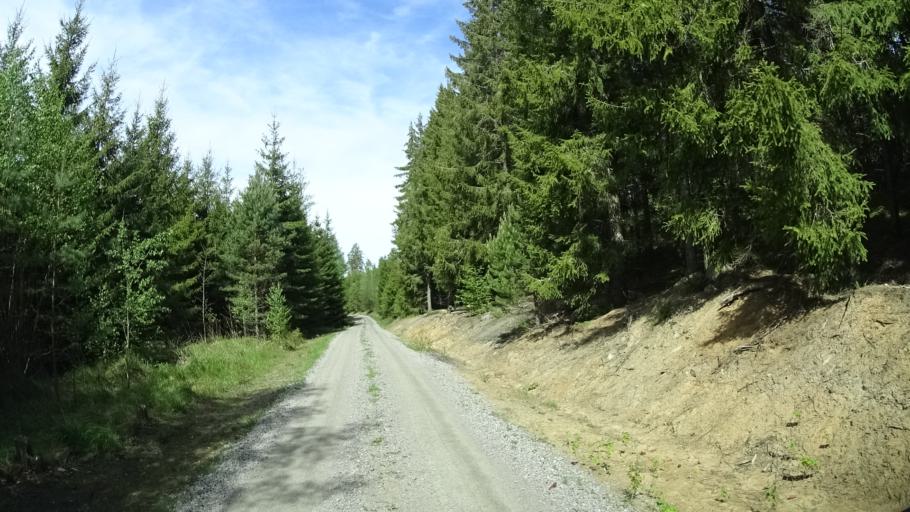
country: SE
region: OEstergoetland
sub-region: Finspangs Kommun
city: Finspang
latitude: 58.7936
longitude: 15.8600
